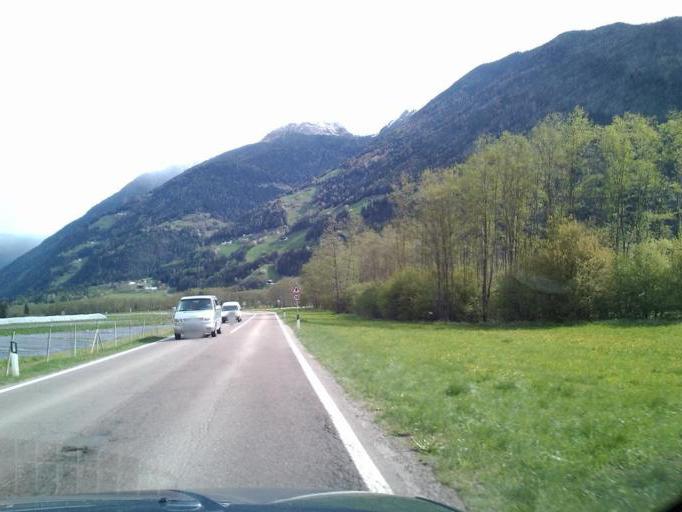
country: IT
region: Trentino-Alto Adige
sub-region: Bolzano
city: Gais
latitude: 46.8457
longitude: 11.9482
